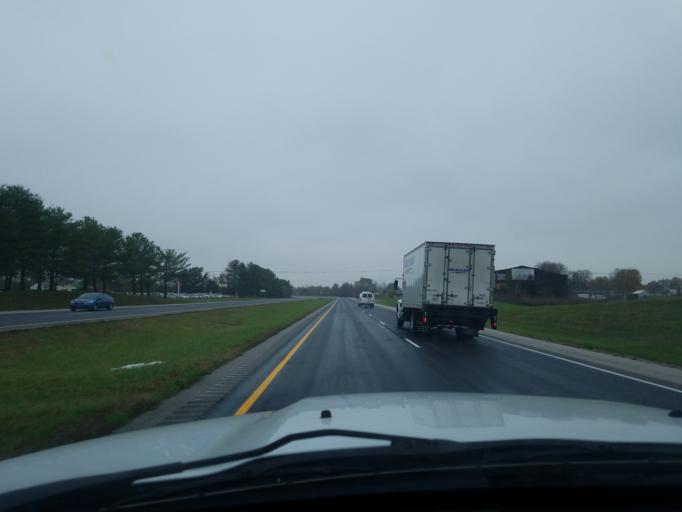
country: US
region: Kentucky
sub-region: Larue County
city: Hodgenville
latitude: 37.5553
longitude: -85.7416
